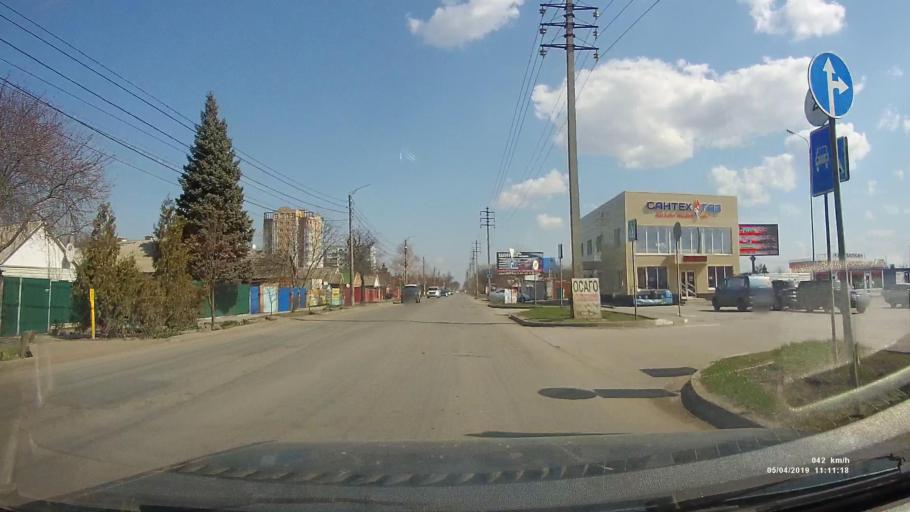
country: RU
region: Rostov
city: Azov
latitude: 47.0943
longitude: 39.4341
